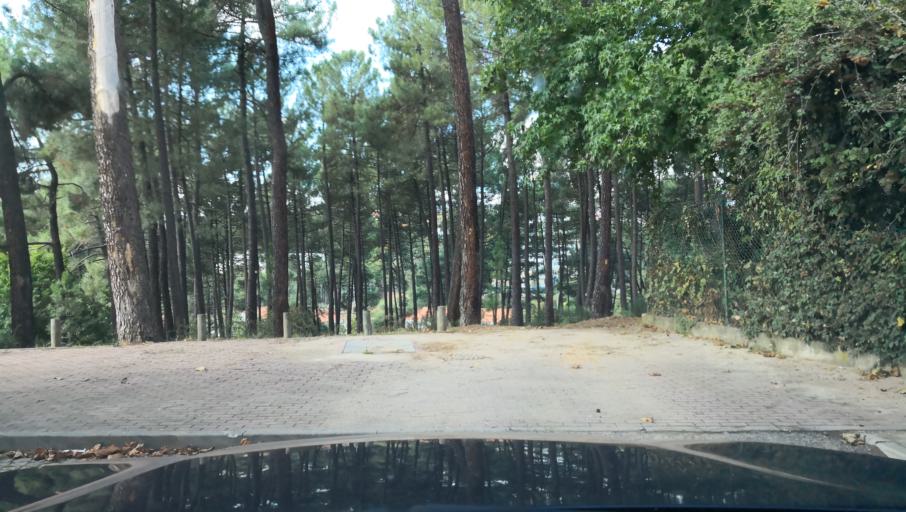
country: PT
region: Vila Real
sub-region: Vila Real
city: Vila Real
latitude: 41.3008
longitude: -7.7335
